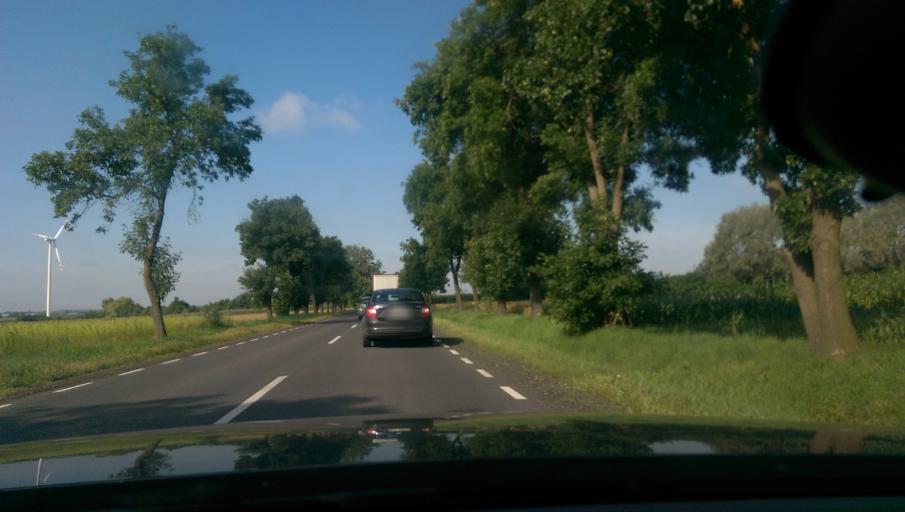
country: PL
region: Masovian Voivodeship
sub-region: Powiat plonski
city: Plonsk
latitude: 52.6454
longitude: 20.4177
